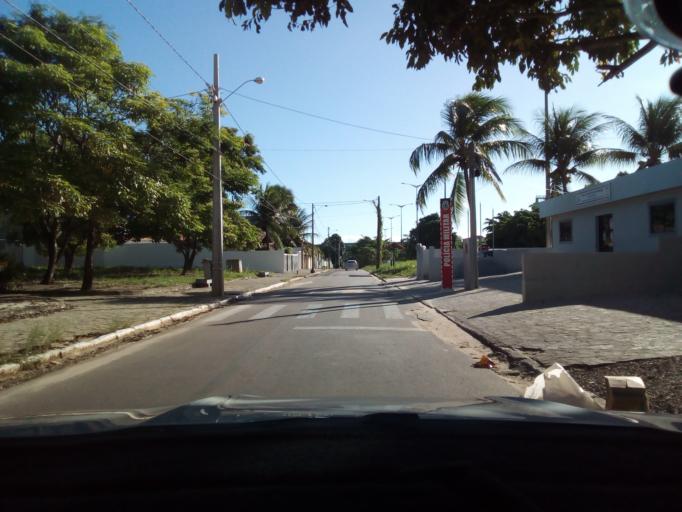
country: BR
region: Paraiba
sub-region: Joao Pessoa
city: Joao Pessoa
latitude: -7.1332
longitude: -34.8301
